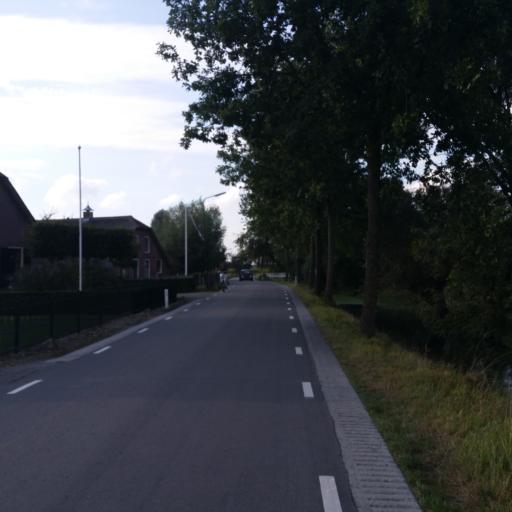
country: NL
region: Utrecht
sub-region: Gemeente IJsselstein
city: IJsselstein
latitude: 52.0412
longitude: 5.0137
